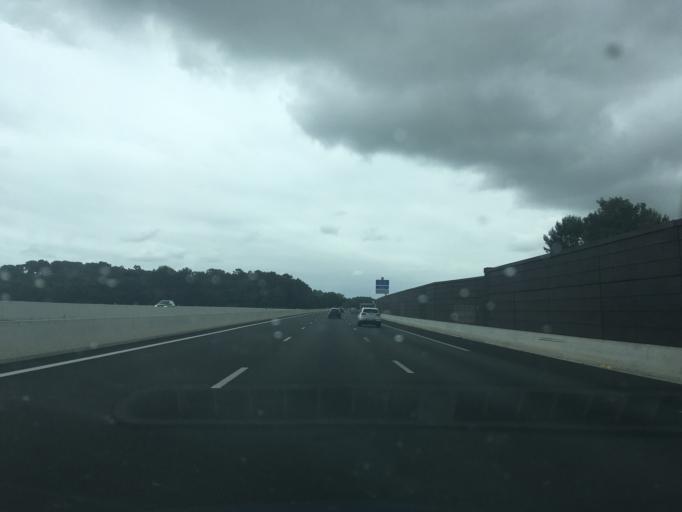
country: FR
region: Aquitaine
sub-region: Departement des Landes
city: Labenne
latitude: 43.6011
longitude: -1.4160
